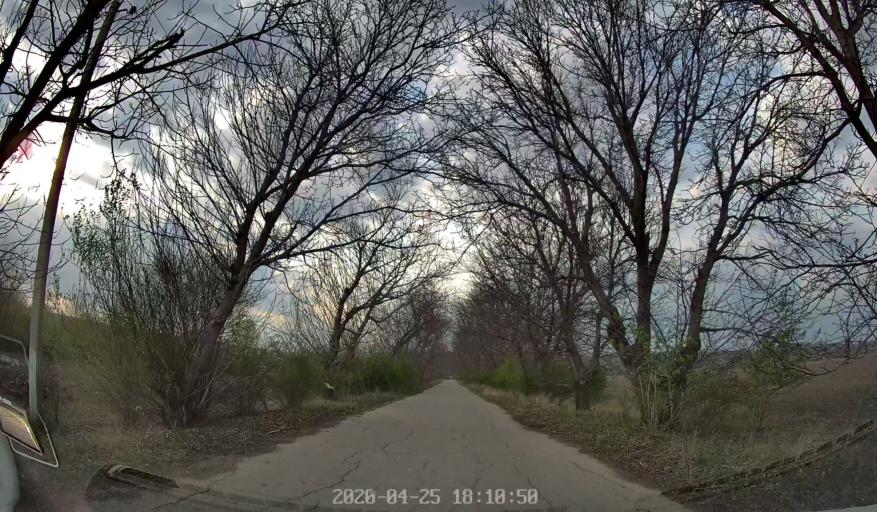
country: MD
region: Chisinau
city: Vadul lui Voda
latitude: 47.1362
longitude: 29.0739
